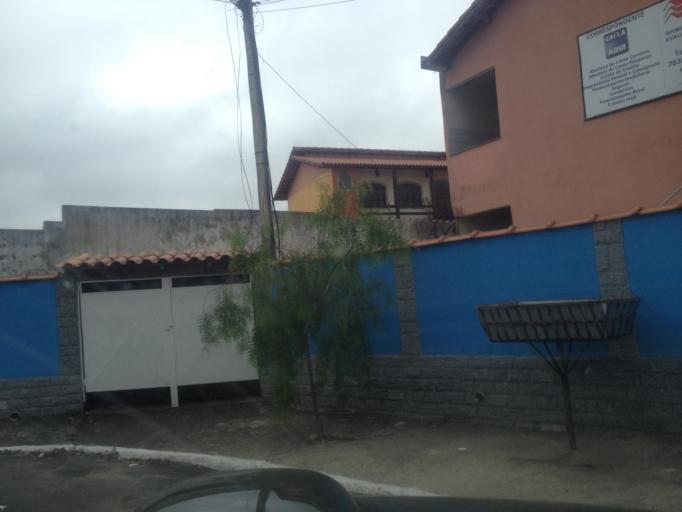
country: BR
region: Rio de Janeiro
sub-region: Porto Real
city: Porto Real
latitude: -22.4134
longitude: -44.3091
